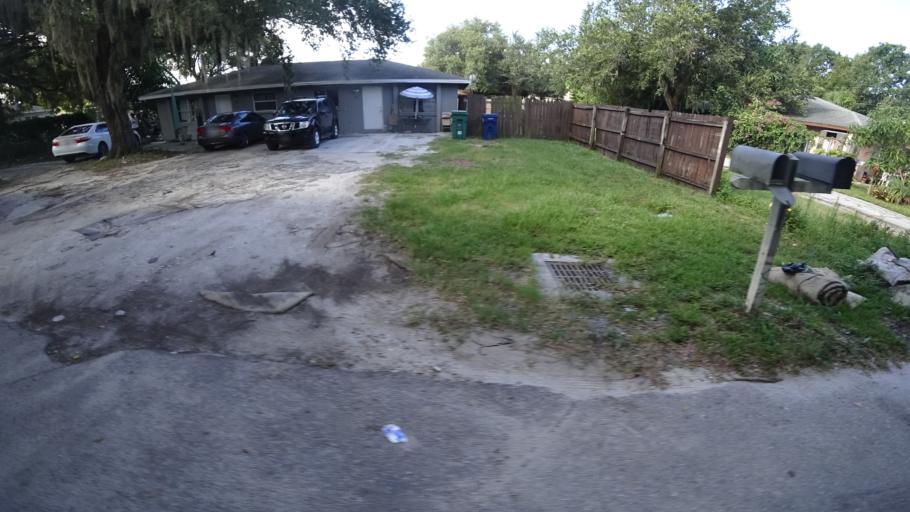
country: US
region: Florida
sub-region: Manatee County
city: Whitfield
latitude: 27.4366
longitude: -82.5565
